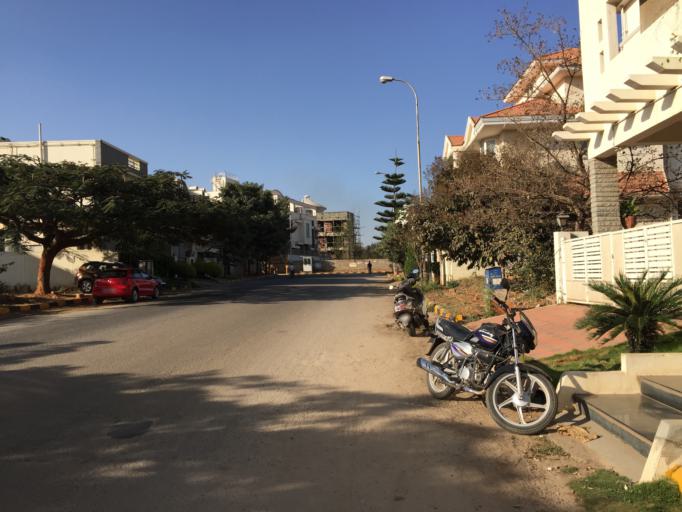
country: IN
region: Karnataka
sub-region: Bangalore Urban
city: Yelahanka
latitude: 13.0544
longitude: 77.6252
